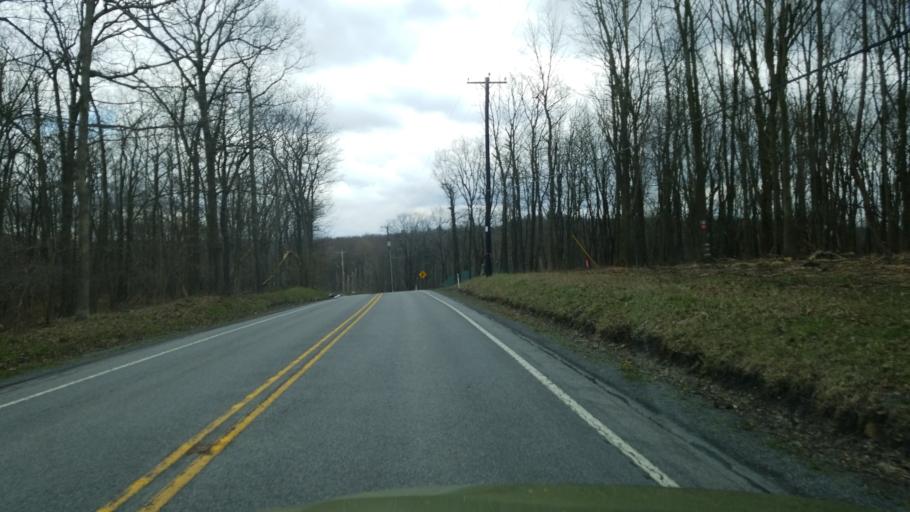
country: US
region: Pennsylvania
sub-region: Blair County
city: Tipton
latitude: 40.7250
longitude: -78.3561
